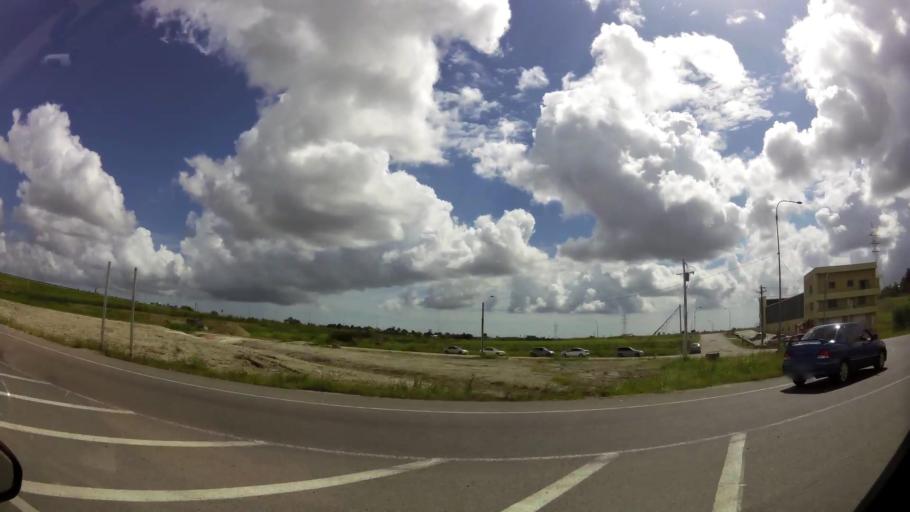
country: TT
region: Penal/Debe
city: Debe
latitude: 10.2173
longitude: -61.4574
